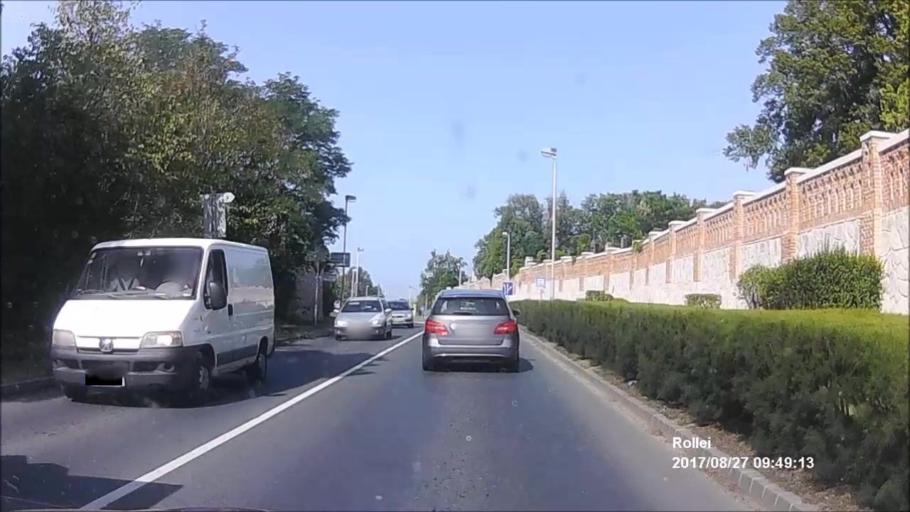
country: HU
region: Gyor-Moson-Sopron
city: Sopron
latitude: 47.6897
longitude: 16.5981
